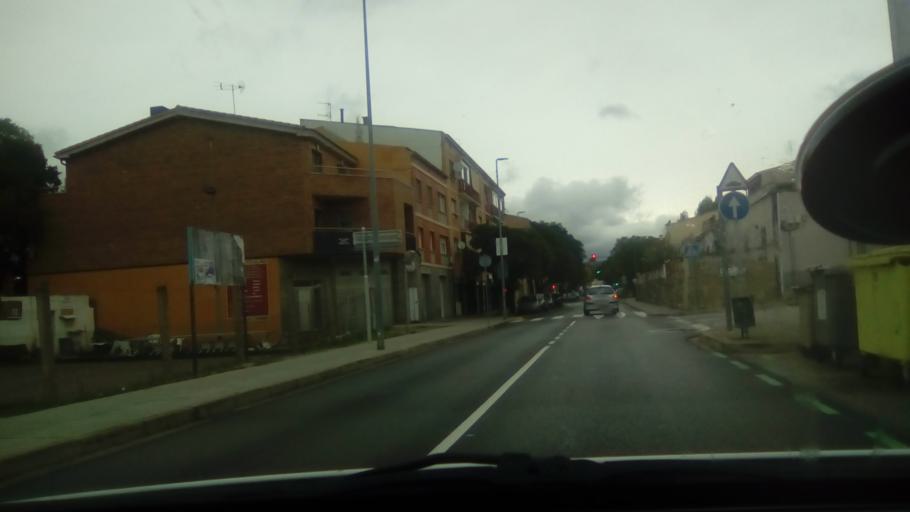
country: ES
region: Catalonia
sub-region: Provincia de Barcelona
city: Monistrol de Montserrat
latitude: 41.6695
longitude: 1.8631
